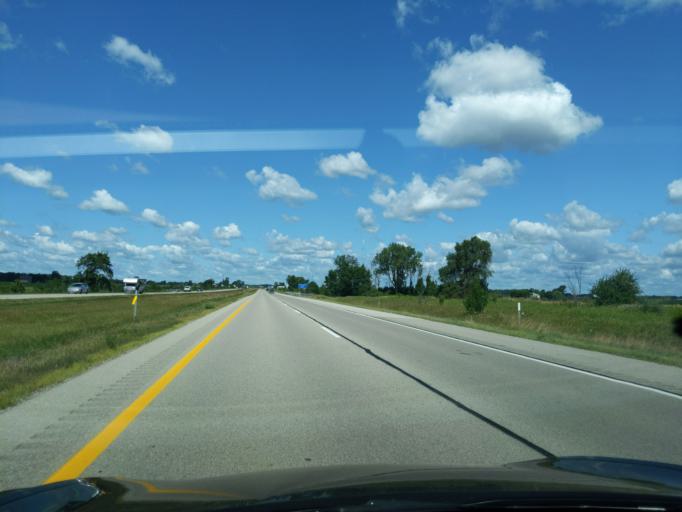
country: US
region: Michigan
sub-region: Isabella County
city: Shepherd
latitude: 43.5465
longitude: -84.6945
